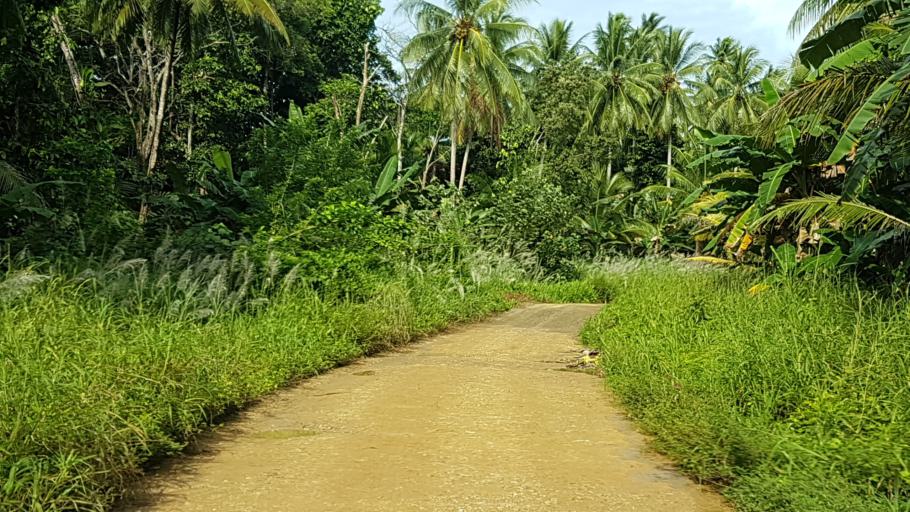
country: PG
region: Milne Bay
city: Alotau
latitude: -10.2628
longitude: 150.8103
